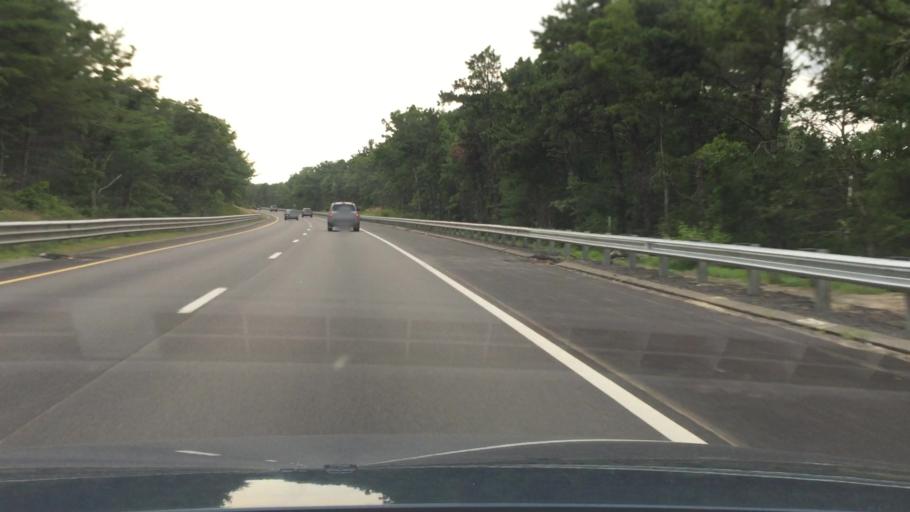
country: US
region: Massachusetts
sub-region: Plymouth County
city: Plymouth
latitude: 41.9293
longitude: -70.6347
